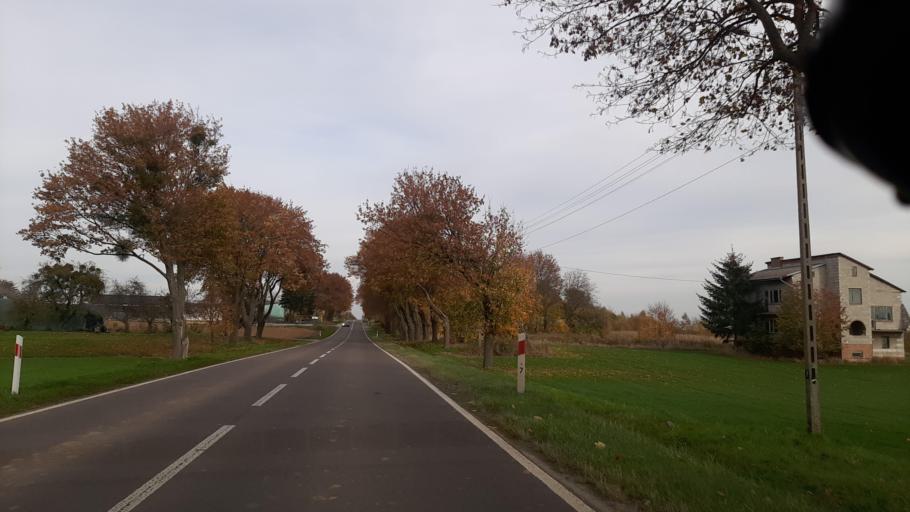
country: PL
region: Lublin Voivodeship
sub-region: Powiat pulawski
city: Markuszow
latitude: 51.3400
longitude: 22.2582
